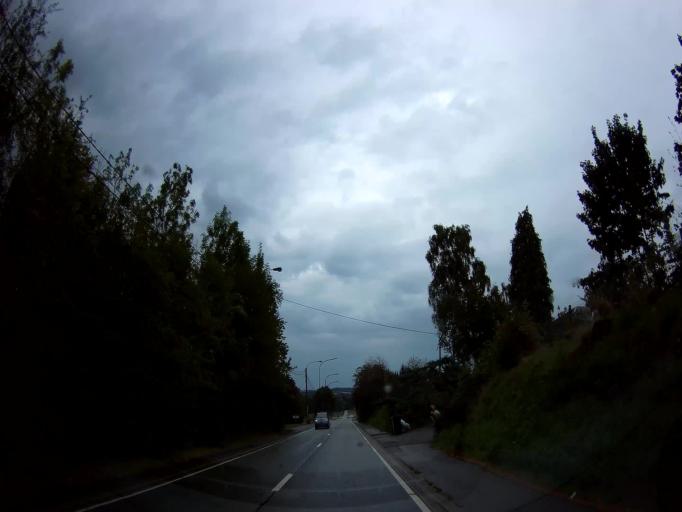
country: BE
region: Wallonia
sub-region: Province de Liege
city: Ferrieres
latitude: 50.4450
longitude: 5.6209
